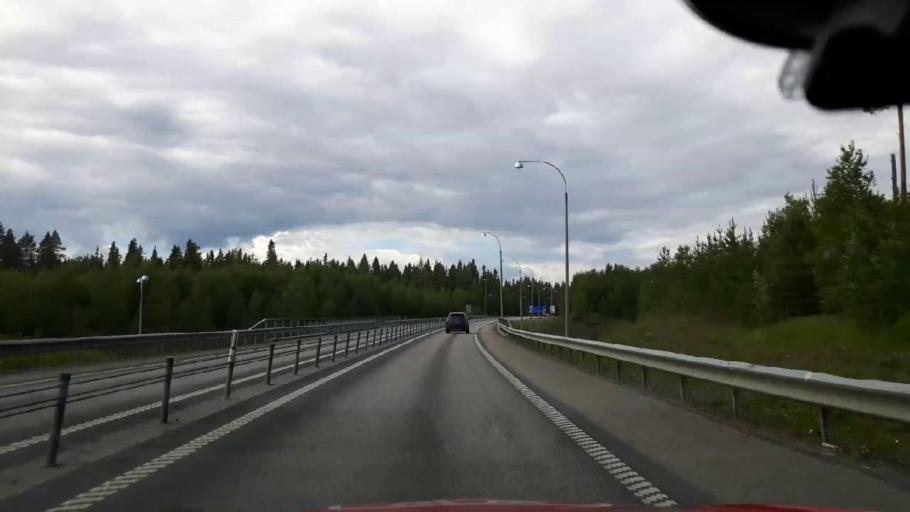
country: SE
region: Jaemtland
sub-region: OEstersunds Kommun
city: Ostersund
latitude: 63.2164
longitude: 14.6351
